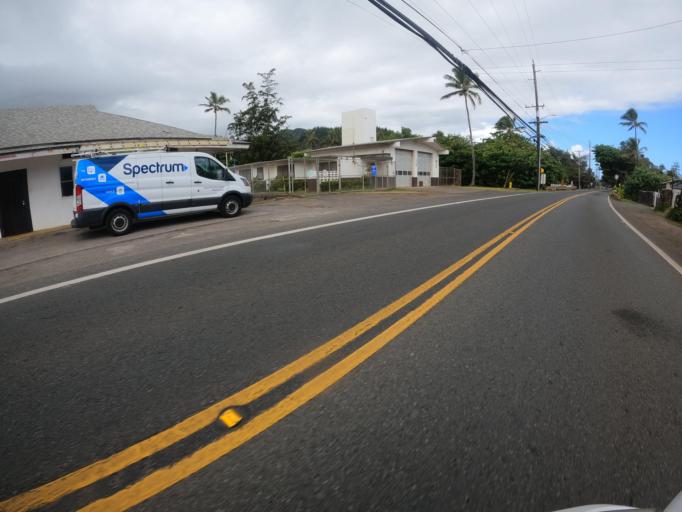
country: US
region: Hawaii
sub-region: Honolulu County
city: Hau'ula
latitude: 21.6080
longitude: -157.9087
